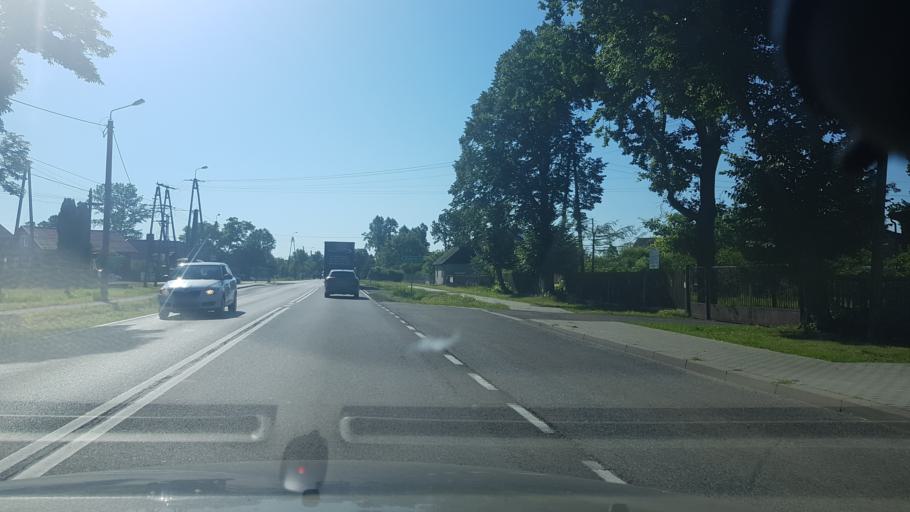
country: PL
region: Masovian Voivodeship
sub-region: Powiat wegrowski
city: Lochow
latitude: 52.5488
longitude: 21.6287
